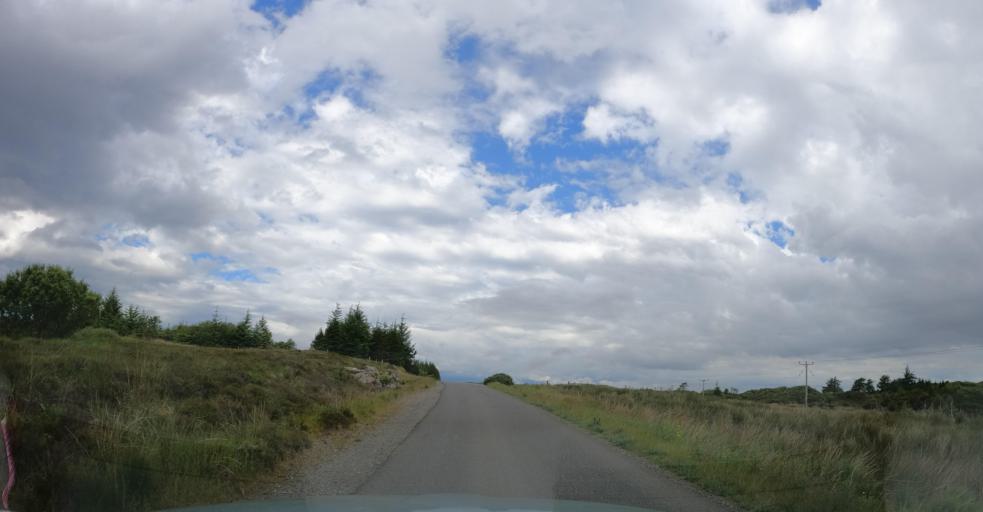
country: GB
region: Scotland
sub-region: Eilean Siar
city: Stornoway
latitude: 58.2029
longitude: -6.4137
